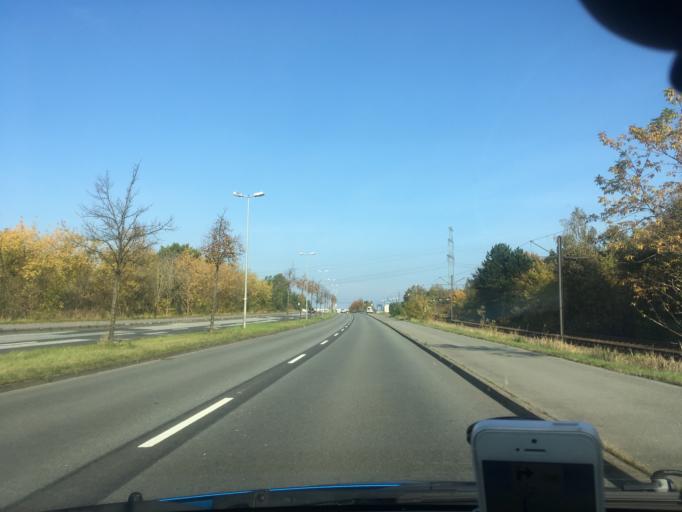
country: DE
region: Mecklenburg-Vorpommern
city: Feldstadt
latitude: 53.5815
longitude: 11.3995
